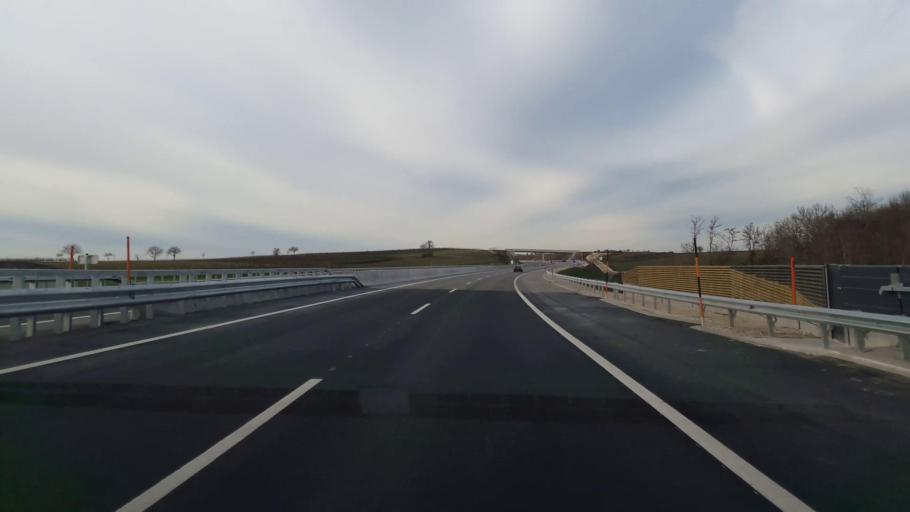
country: AT
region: Lower Austria
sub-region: Politischer Bezirk Mistelbach
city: Herrnbaumgarten
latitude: 48.6683
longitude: 16.6783
